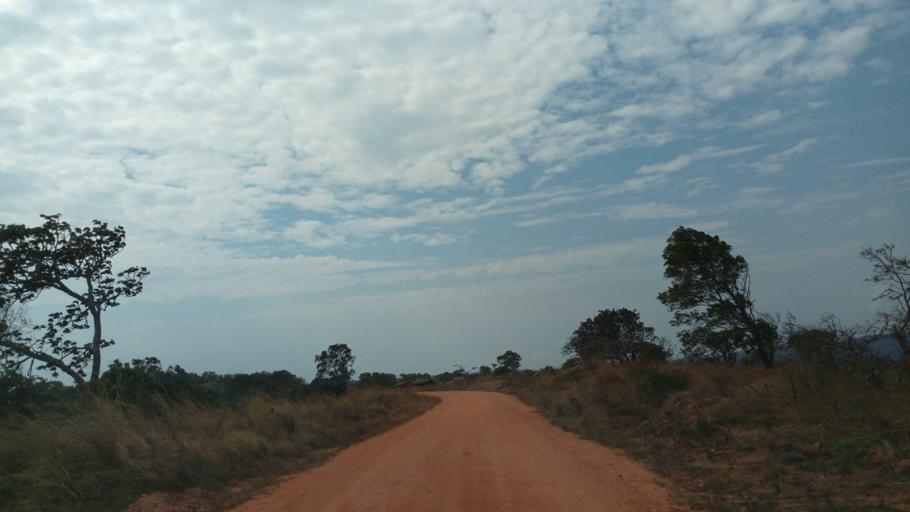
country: CD
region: Katanga
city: Kalemie
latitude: -6.0951
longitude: 28.8873
